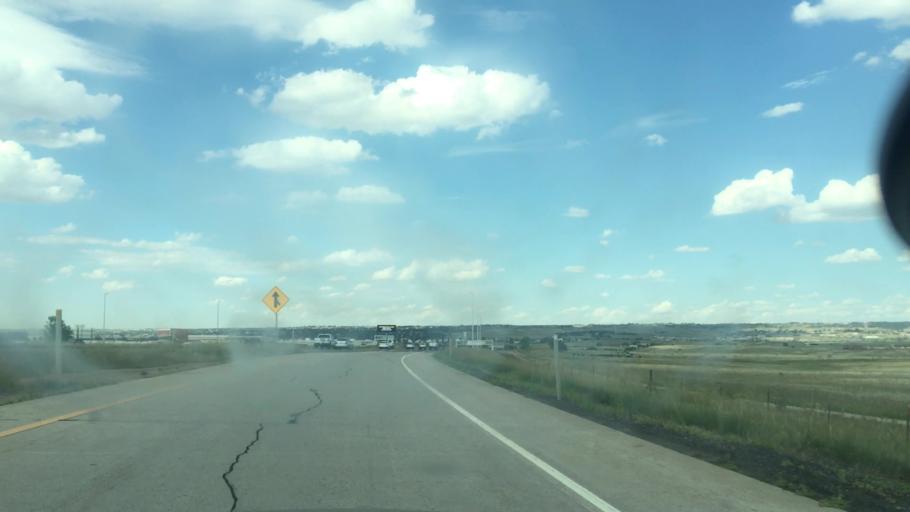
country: US
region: Colorado
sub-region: Douglas County
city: Meridian
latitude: 39.5528
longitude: -104.8357
